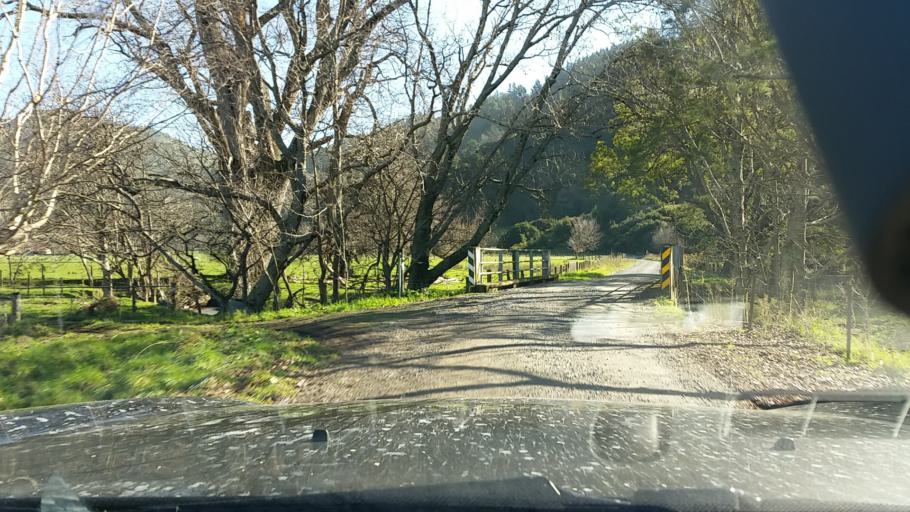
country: NZ
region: Marlborough
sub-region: Marlborough District
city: Blenheim
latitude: -41.4599
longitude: 173.7865
